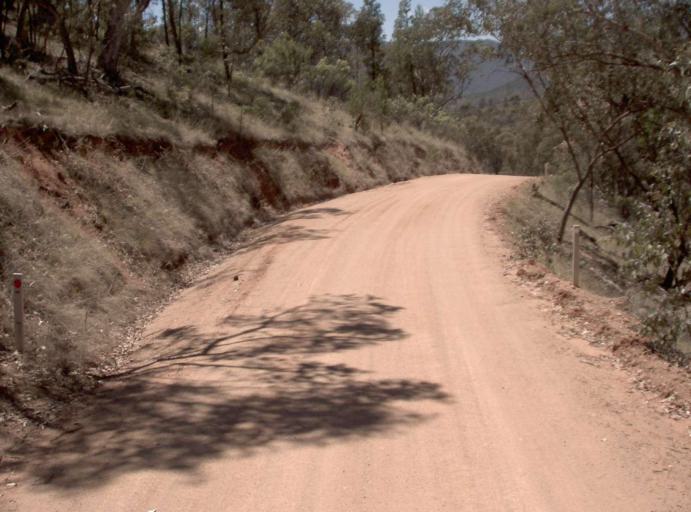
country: AU
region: New South Wales
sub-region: Snowy River
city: Jindabyne
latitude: -36.9254
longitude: 148.3782
